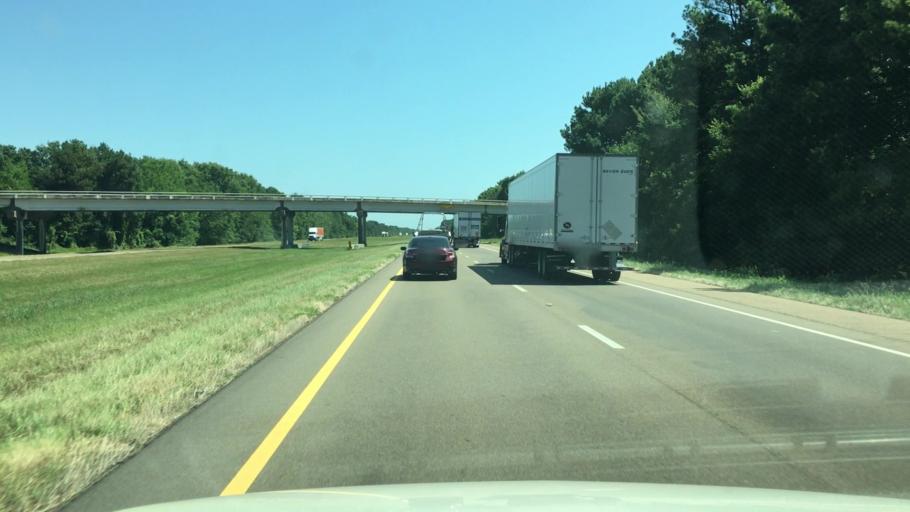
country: US
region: Texas
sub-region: Morris County
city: Naples
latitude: 33.3341
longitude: -94.6697
